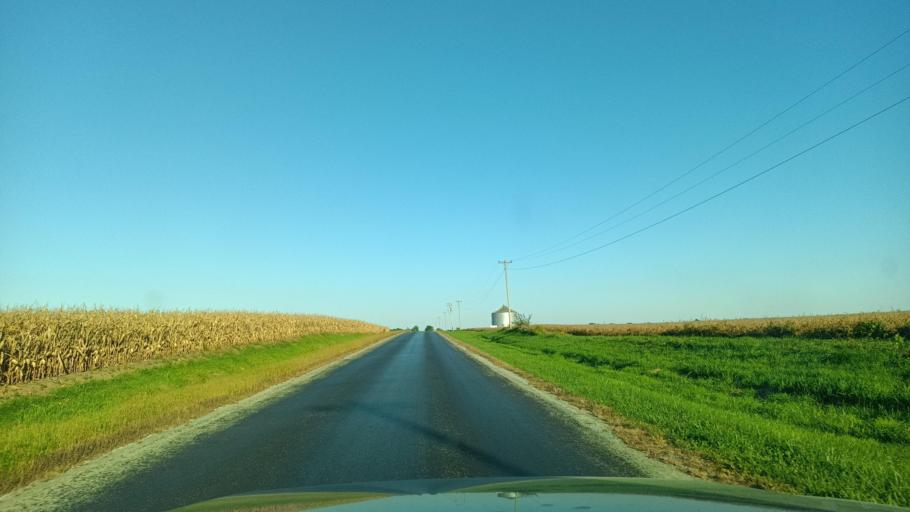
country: US
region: Illinois
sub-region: Warren County
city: Monmouth
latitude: 40.9860
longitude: -90.6233
